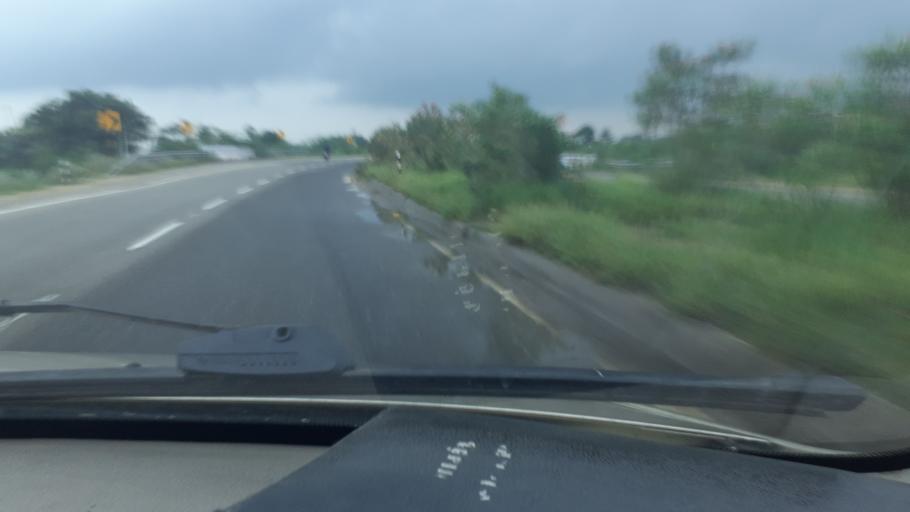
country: IN
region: Tamil Nadu
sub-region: Thoothukkudi
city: Kovilpatti
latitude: 9.1307
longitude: 77.8251
